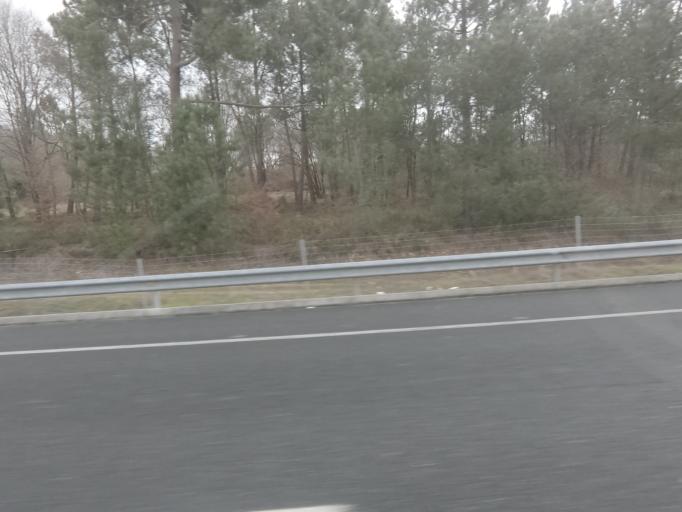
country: ES
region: Galicia
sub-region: Provincia de Pontevedra
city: Lalin
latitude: 42.6717
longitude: -8.1569
